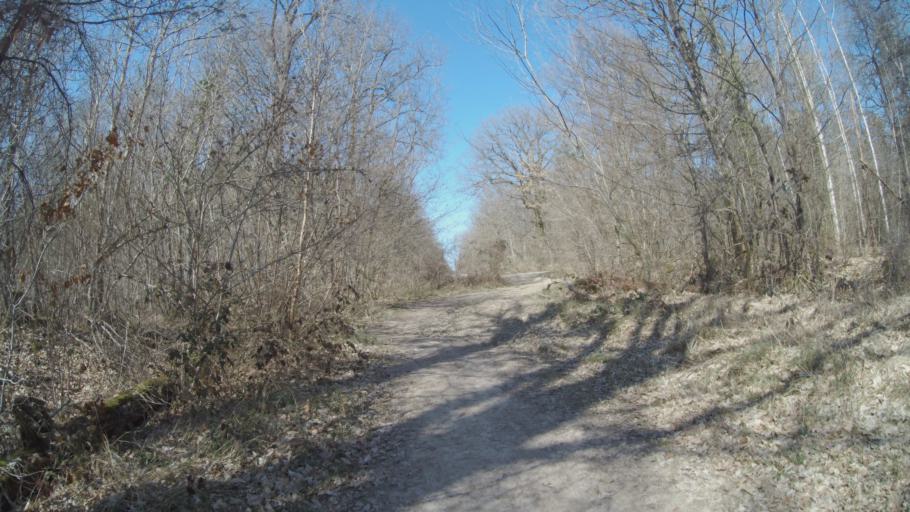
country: FR
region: Centre
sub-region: Departement du Loiret
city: Chanteau
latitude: 47.9492
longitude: 1.9820
